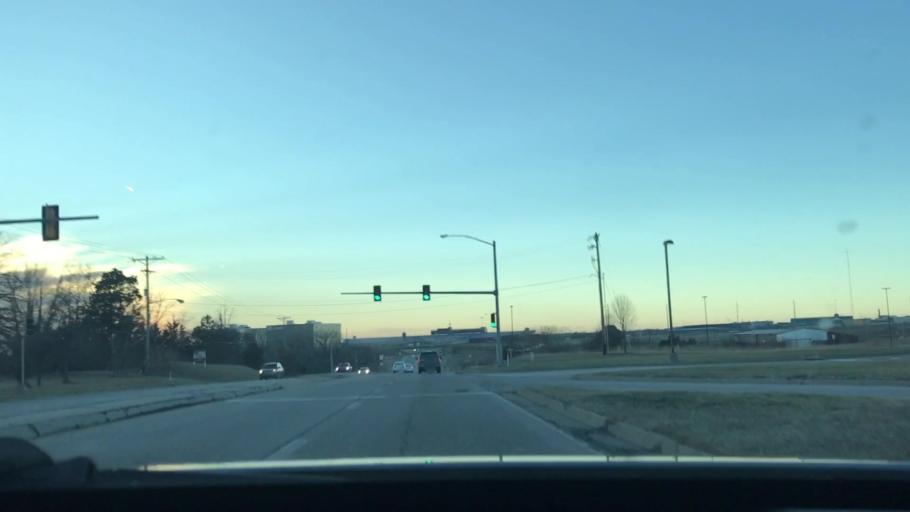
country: US
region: Kansas
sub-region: Wyandotte County
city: Edwardsville
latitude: 39.1165
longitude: -94.8016
